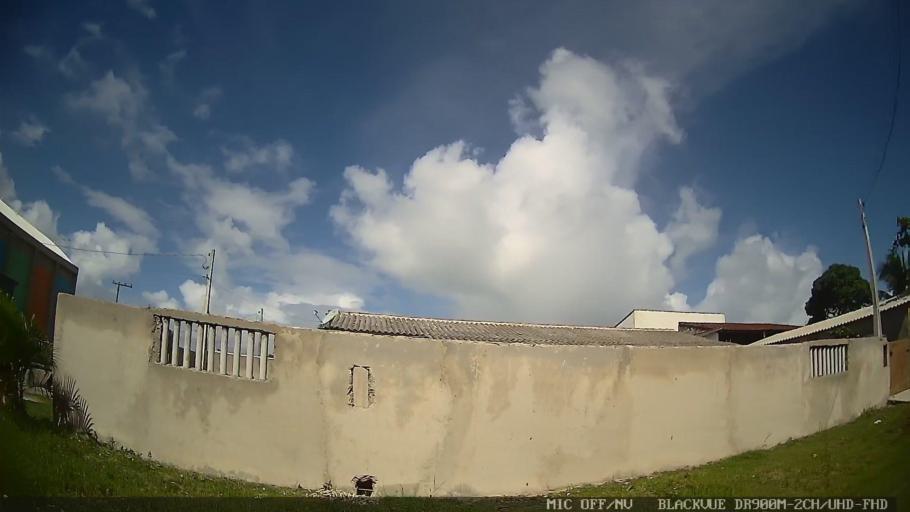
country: BR
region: Sao Paulo
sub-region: Itanhaem
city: Itanhaem
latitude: -24.2416
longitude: -46.8974
